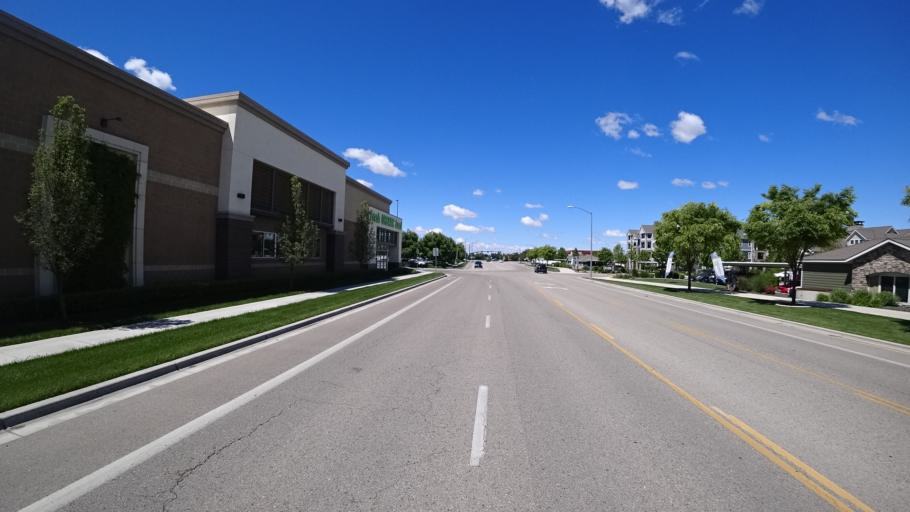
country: US
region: Idaho
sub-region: Ada County
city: Meridian
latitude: 43.6266
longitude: -116.3514
